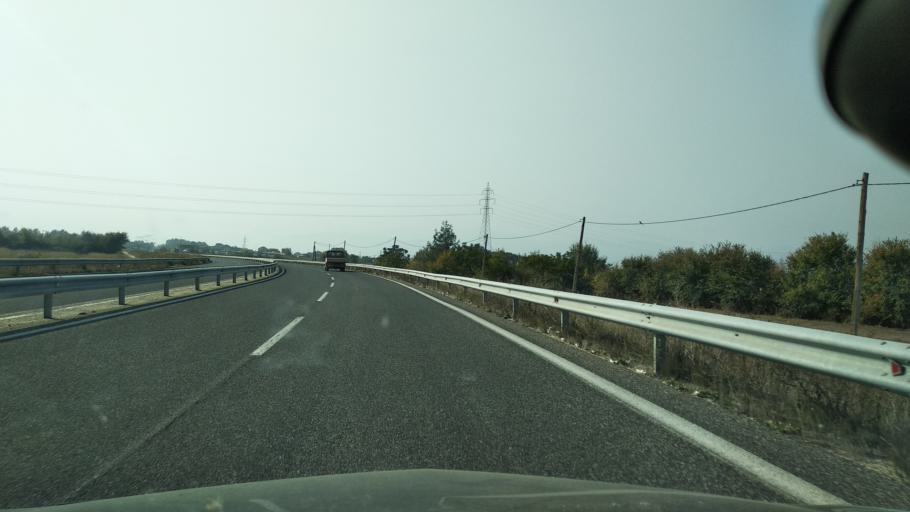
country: GR
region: Thessaly
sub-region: Trikala
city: Trikala
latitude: 39.5633
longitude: 21.8025
